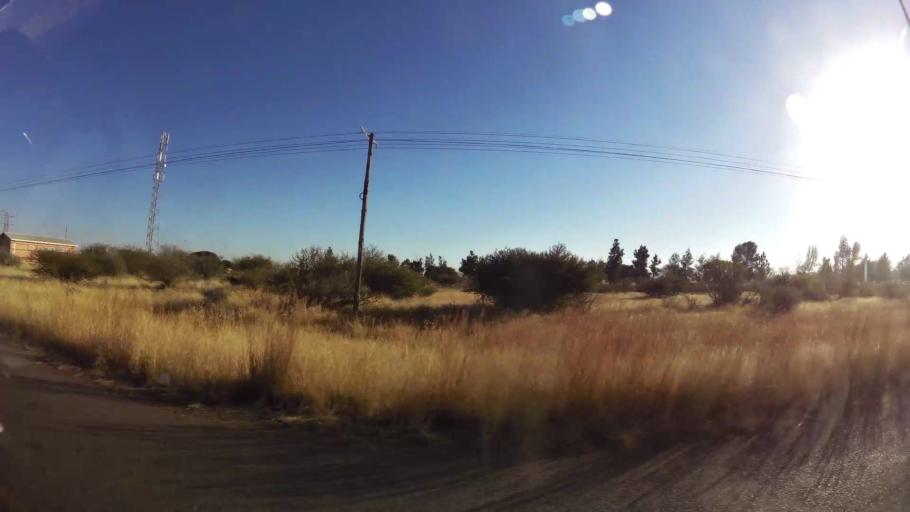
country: ZA
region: Northern Cape
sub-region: Frances Baard District Municipality
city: Kimberley
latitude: -28.7431
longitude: 24.7164
